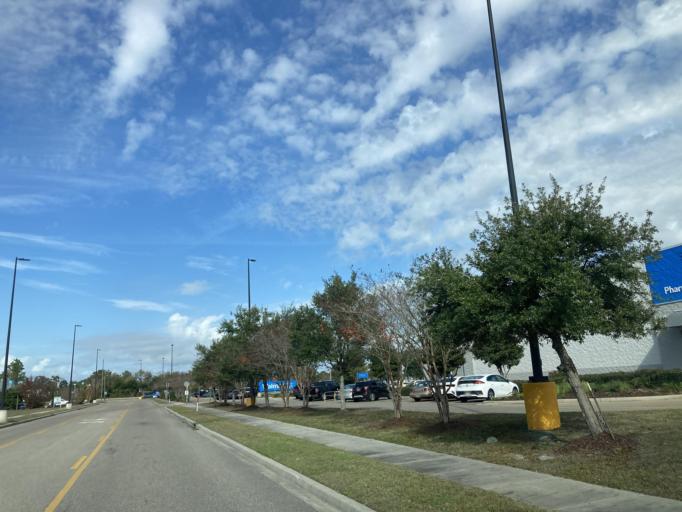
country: US
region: Mississippi
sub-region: Harrison County
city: West Gulfport
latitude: 30.3921
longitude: -88.9962
